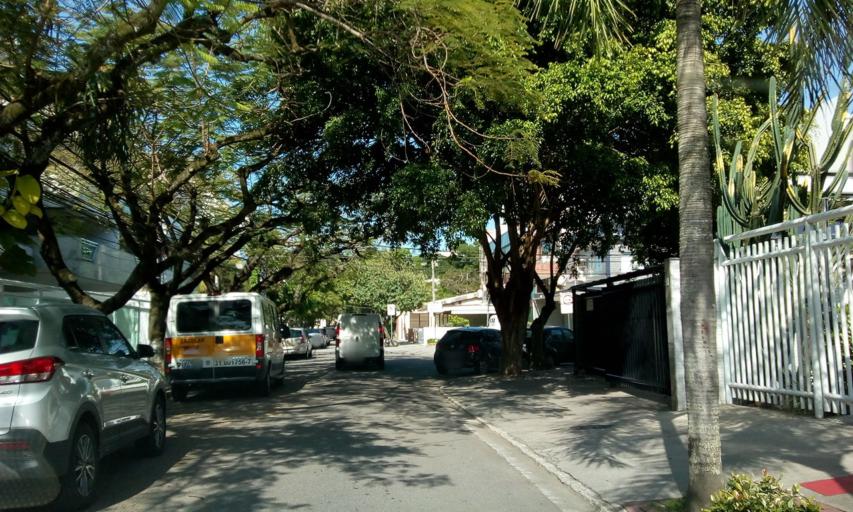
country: BR
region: Rio de Janeiro
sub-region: Nilopolis
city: Nilopolis
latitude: -23.0178
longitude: -43.4582
